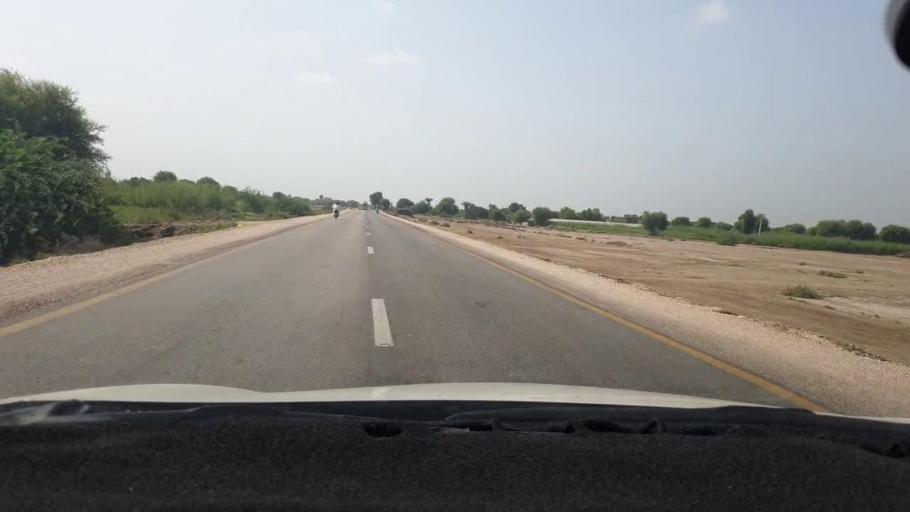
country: PK
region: Sindh
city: Mirpur Khas
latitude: 25.6357
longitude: 69.0934
